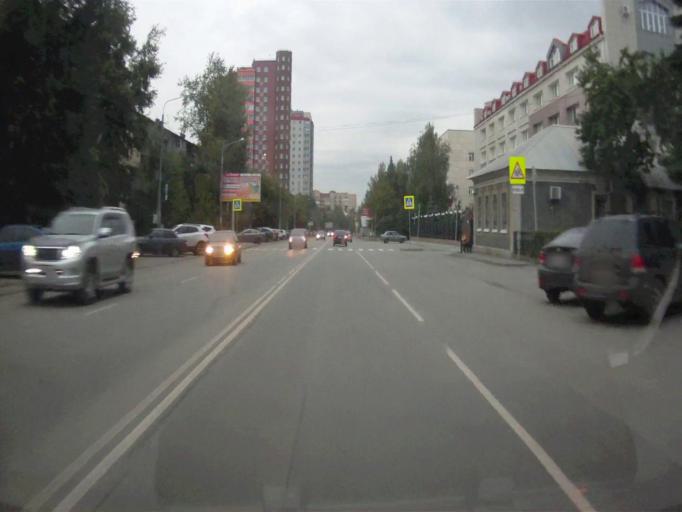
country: RU
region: Chelyabinsk
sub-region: Gorod Chelyabinsk
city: Chelyabinsk
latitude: 55.1496
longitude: 61.3986
